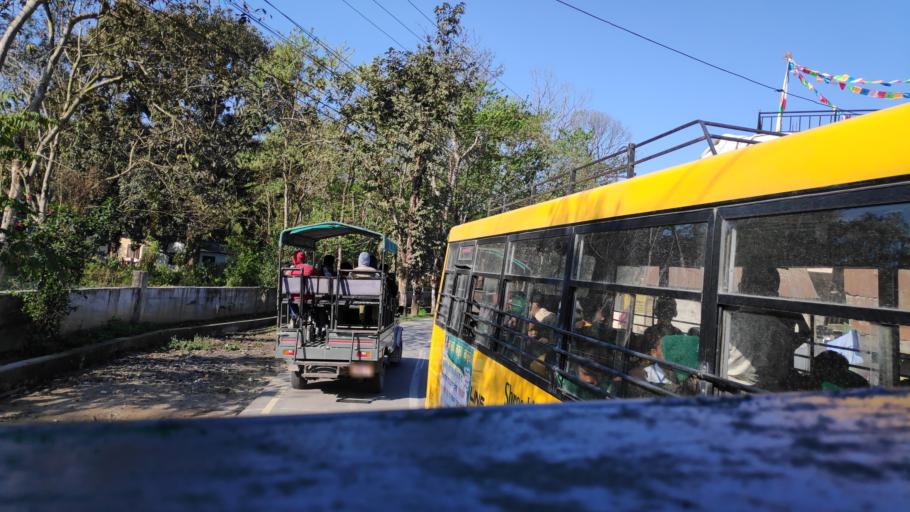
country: NP
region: Central Region
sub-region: Narayani Zone
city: Bharatpur
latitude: 27.5744
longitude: 84.5015
